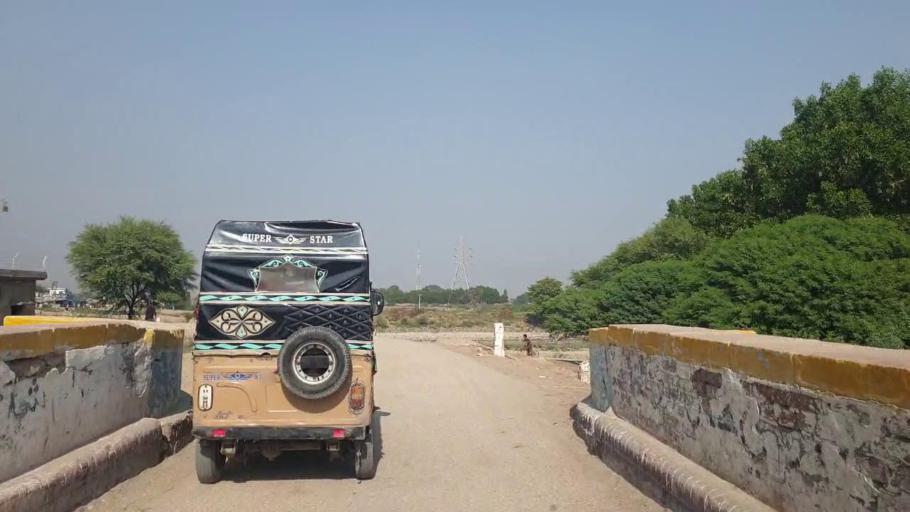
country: PK
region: Sindh
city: Jamshoro
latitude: 25.4392
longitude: 68.3335
